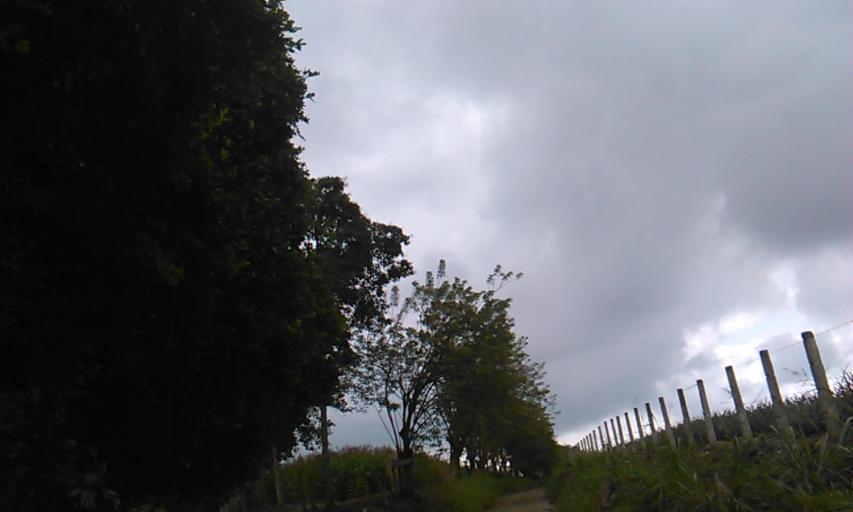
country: CO
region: Quindio
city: La Tebaida
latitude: 4.5041
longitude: -75.8571
